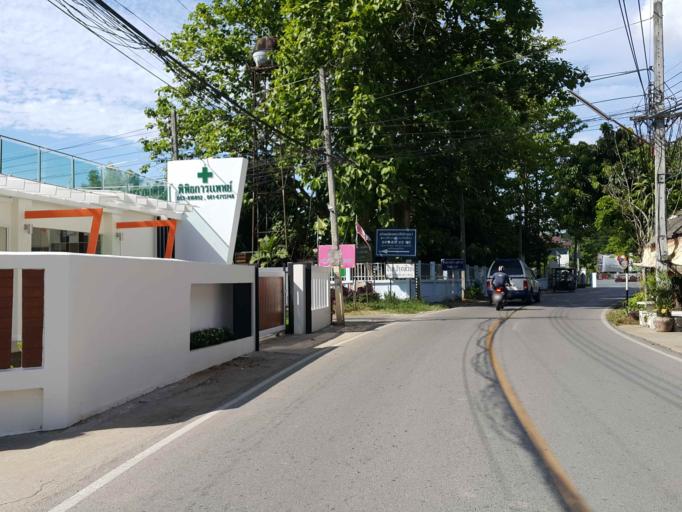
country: TH
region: Chiang Mai
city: Saraphi
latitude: 18.7339
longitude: 98.9894
